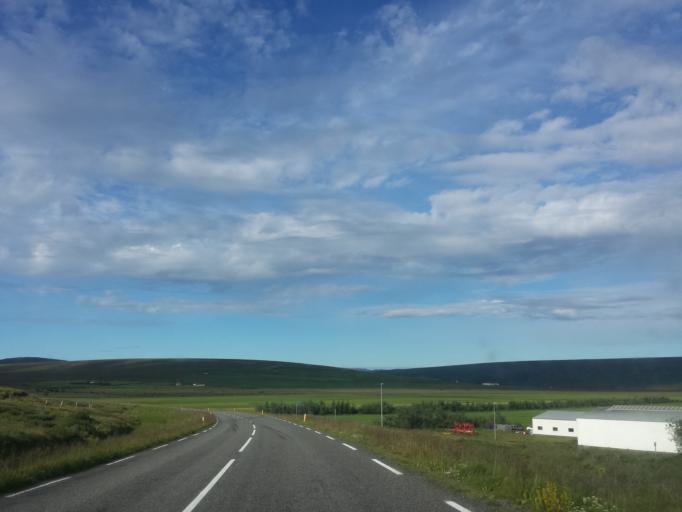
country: IS
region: Northeast
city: Laugar
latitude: 65.7125
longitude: -17.6057
